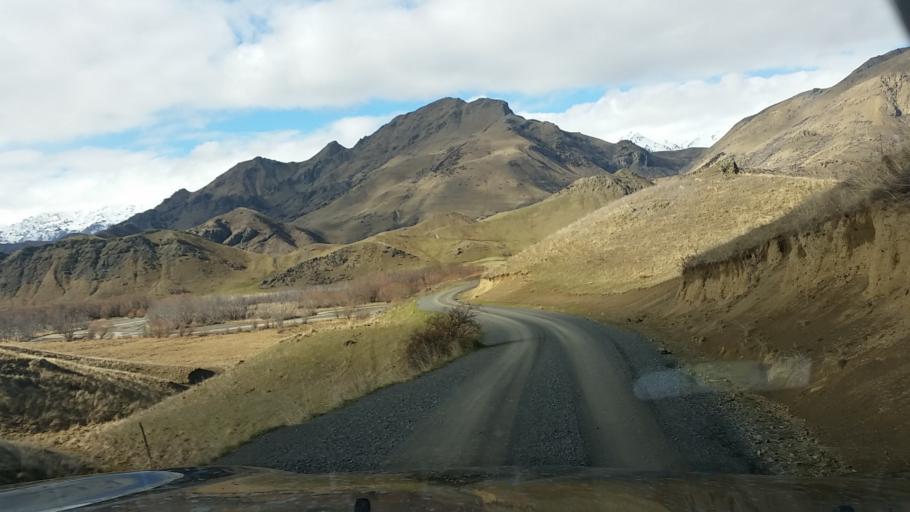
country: NZ
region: Canterbury
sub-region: Kaikoura District
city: Kaikoura
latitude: -42.0408
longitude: 173.3759
